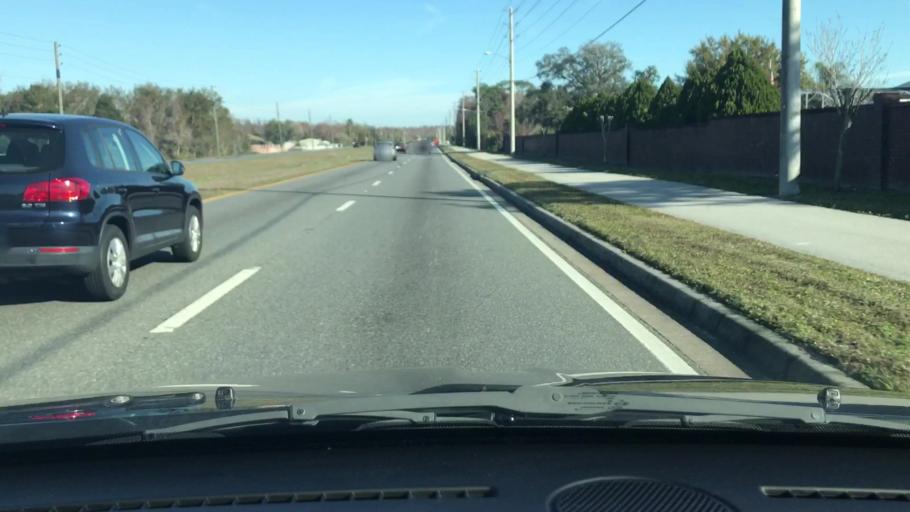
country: US
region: Florida
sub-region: Osceola County
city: Campbell
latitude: 28.2159
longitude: -81.4401
